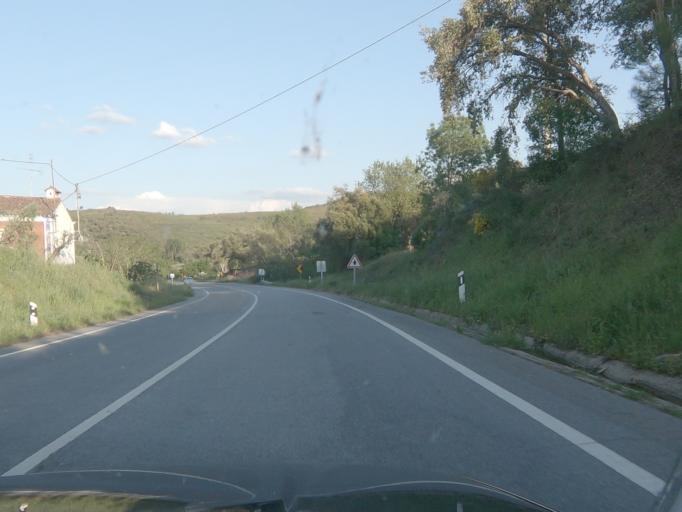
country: PT
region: Portalegre
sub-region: Portalegre
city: Sao Juliao
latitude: 39.3645
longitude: -7.3346
